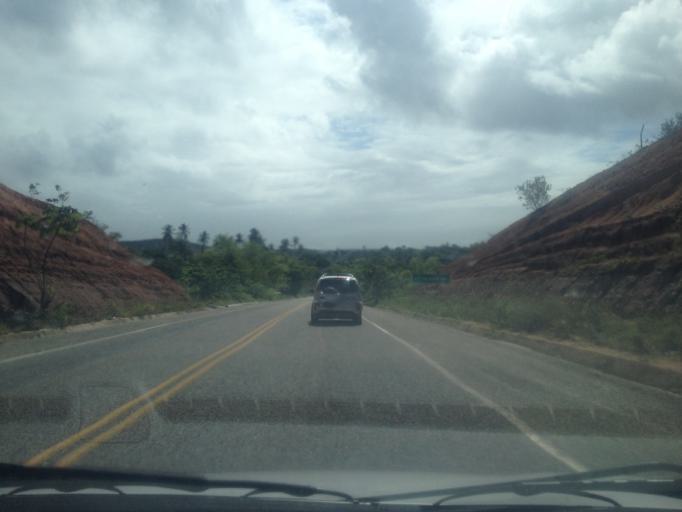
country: BR
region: Bahia
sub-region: Conde
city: Conde
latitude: -11.7155
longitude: -37.5722
